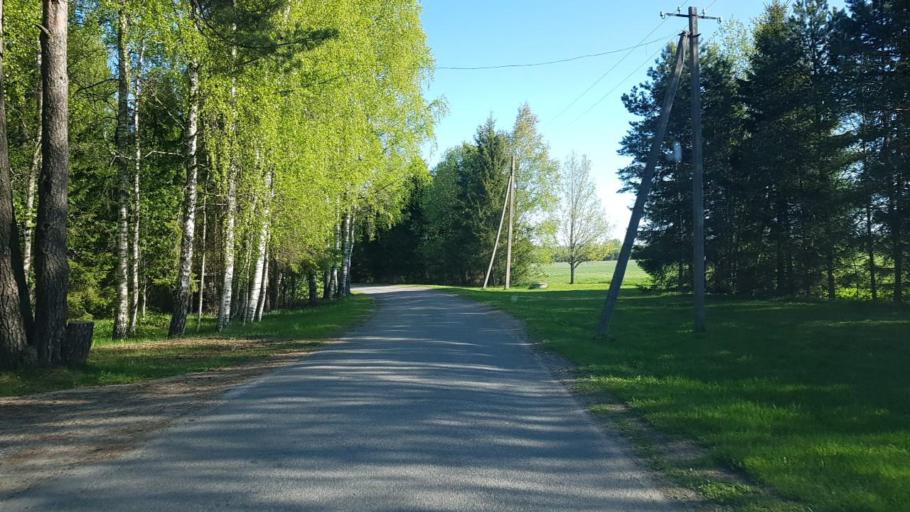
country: EE
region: Laeaene-Virumaa
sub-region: Viru-Nigula vald
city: Kunda
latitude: 59.3294
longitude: 26.6361
